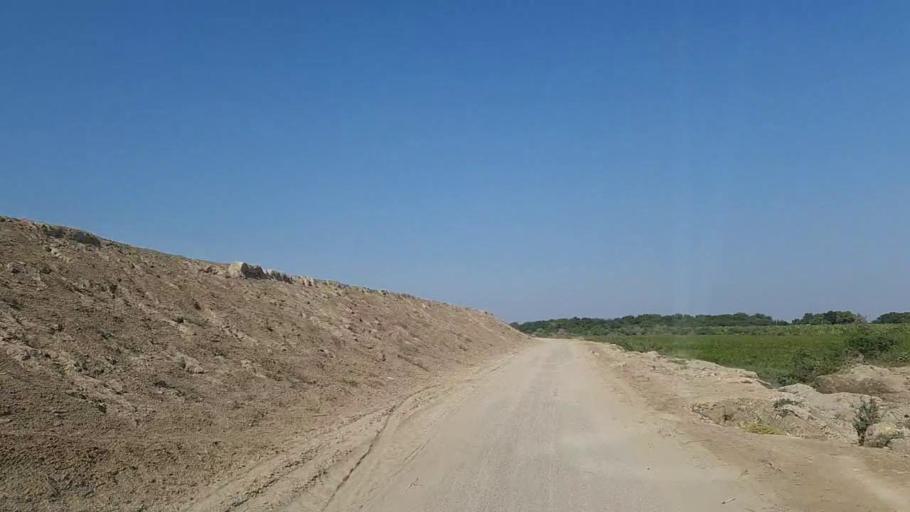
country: PK
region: Sindh
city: Chuhar Jamali
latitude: 24.5667
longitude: 68.0295
